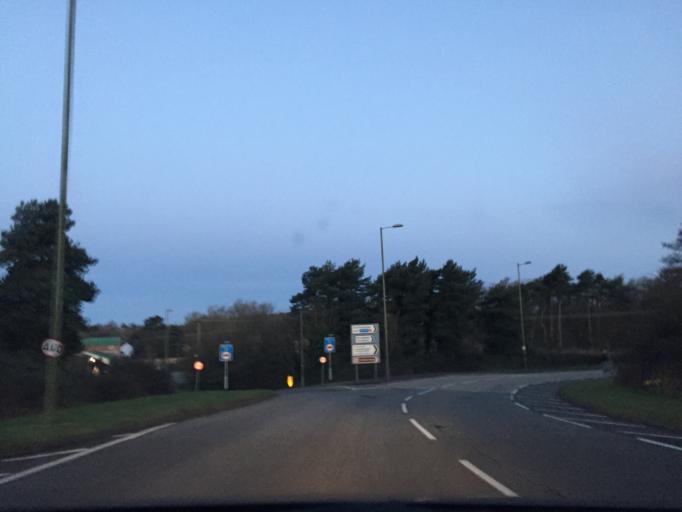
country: GB
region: England
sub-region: Hampshire
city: Fareham
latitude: 50.8503
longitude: -1.2288
